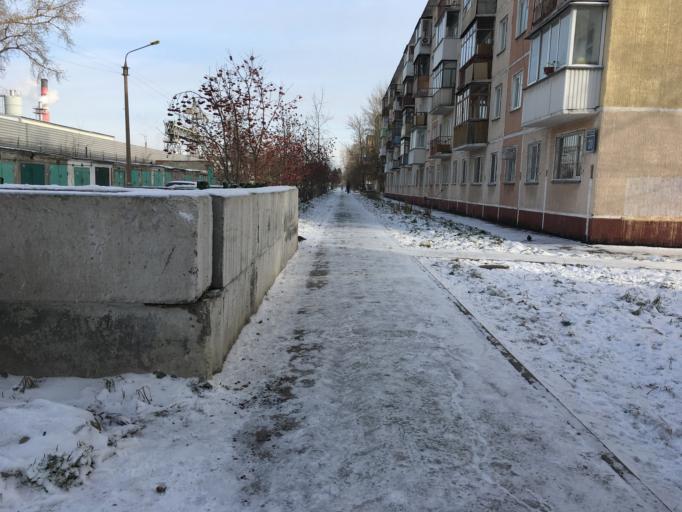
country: RU
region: Novosibirsk
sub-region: Novosibirskiy Rayon
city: Novosibirsk
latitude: 55.0565
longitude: 82.9699
